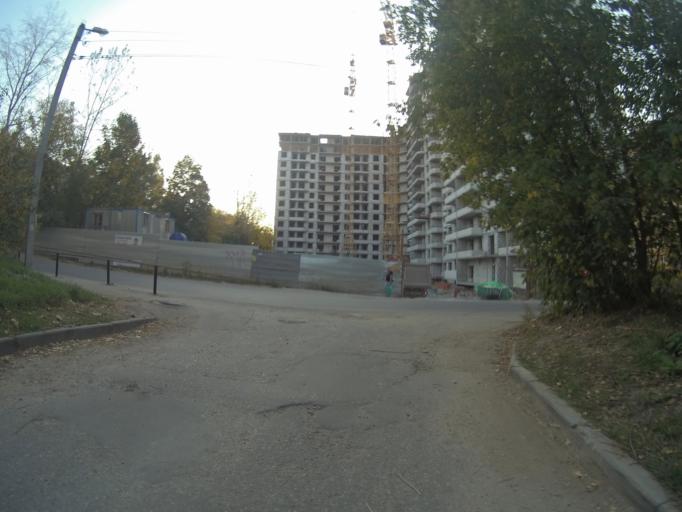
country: RU
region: Vladimir
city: Vladimir
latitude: 56.1177
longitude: 40.3471
